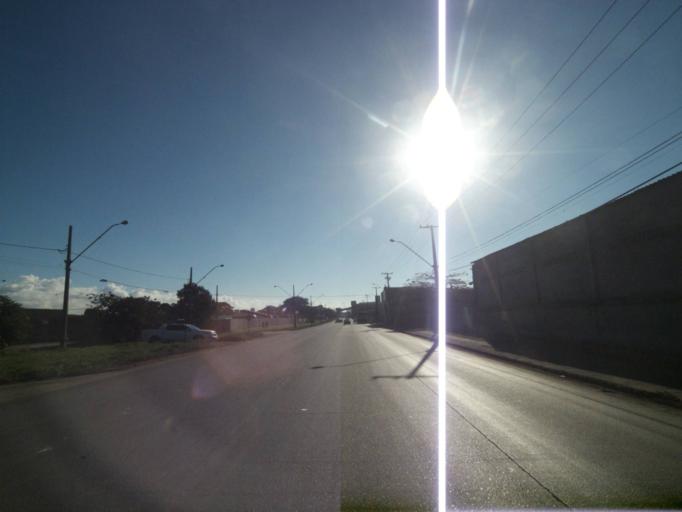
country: BR
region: Parana
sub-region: Paranagua
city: Paranagua
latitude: -25.5140
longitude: -48.5218
